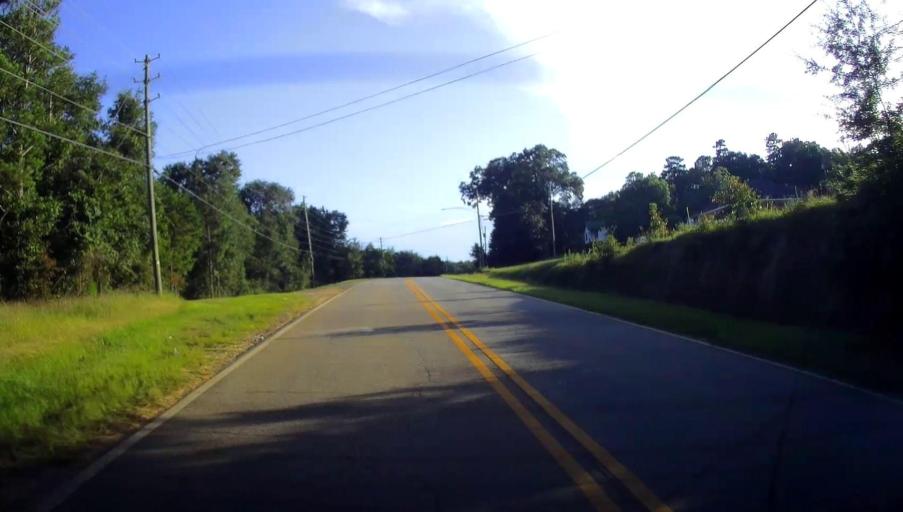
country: US
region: Georgia
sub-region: Muscogee County
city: Columbus
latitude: 32.4282
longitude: -85.0142
